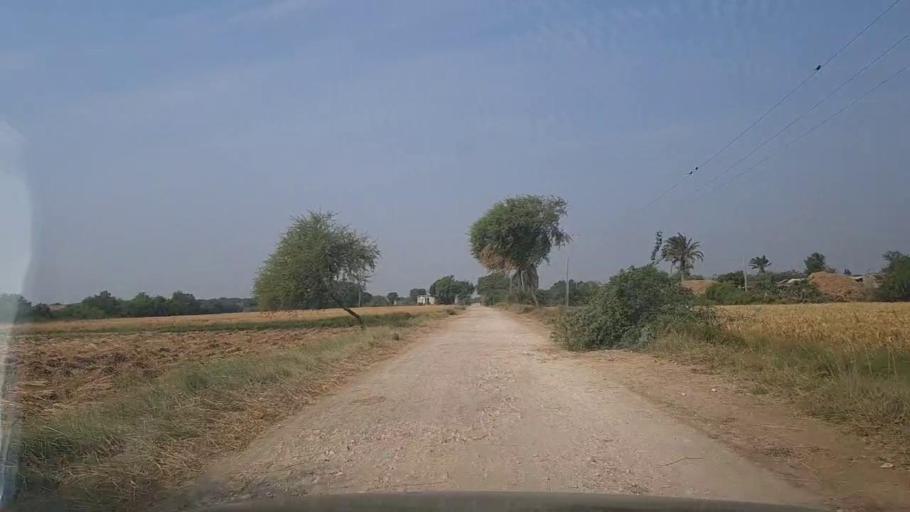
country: PK
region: Sindh
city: Bulri
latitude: 24.9767
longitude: 68.3009
